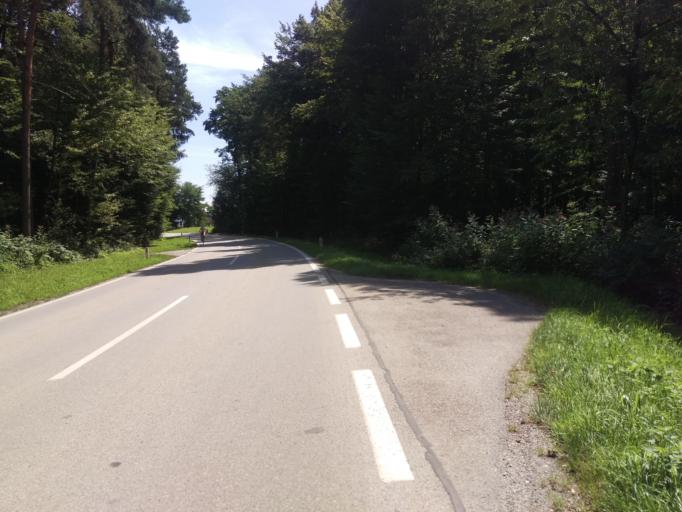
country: AT
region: Styria
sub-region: Politischer Bezirk Graz-Umgebung
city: Zettling
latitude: 46.9696
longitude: 15.4409
